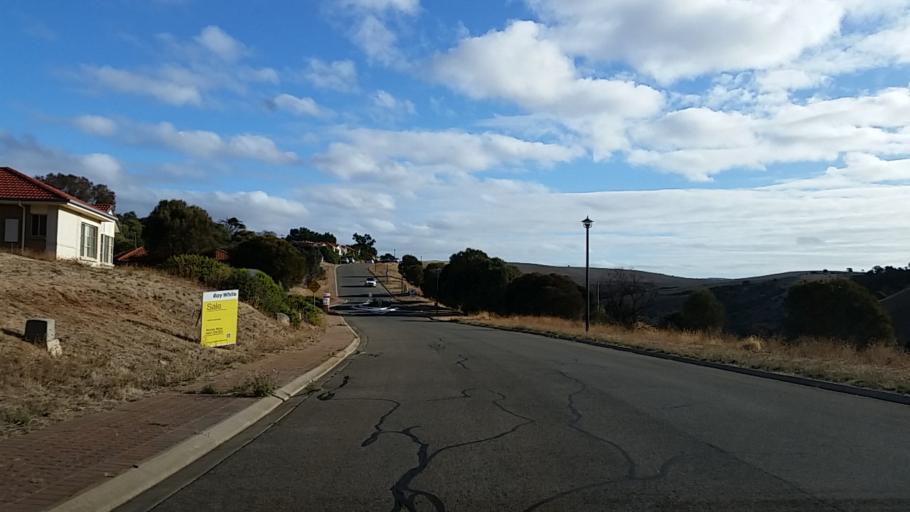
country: AU
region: South Australia
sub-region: Yankalilla
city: Normanville
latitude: -35.5008
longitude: 138.2509
